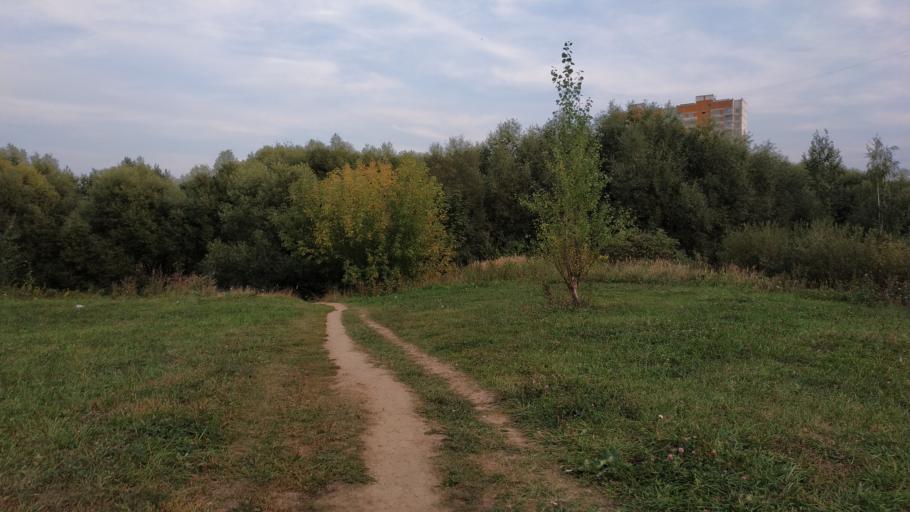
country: RU
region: Moscow
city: Solntsevo
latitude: 55.6416
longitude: 37.3742
